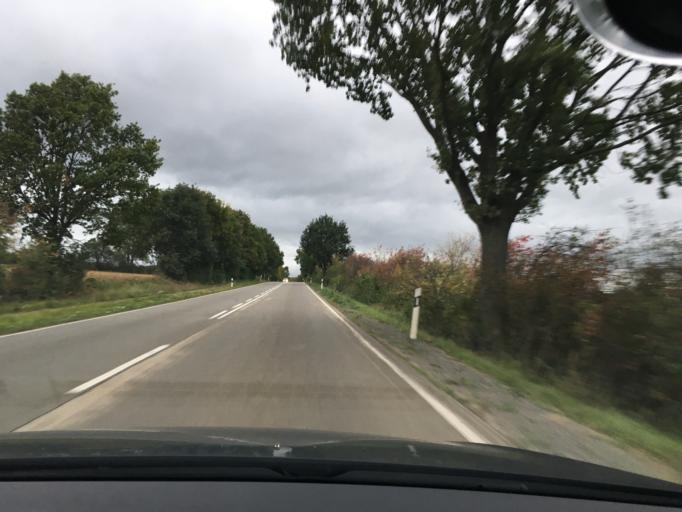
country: DE
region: North Rhine-Westphalia
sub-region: Regierungsbezirk Koln
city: Kreuzau
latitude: 50.7443
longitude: 6.5445
